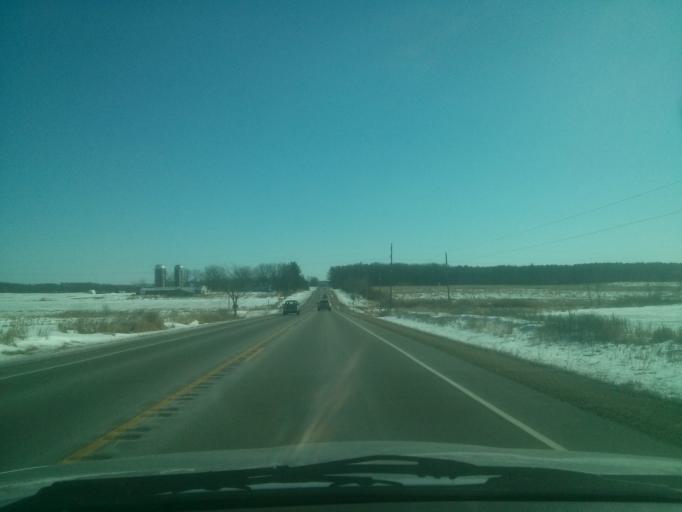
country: US
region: Wisconsin
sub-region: Polk County
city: Clear Lake
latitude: 45.1364
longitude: -92.2940
